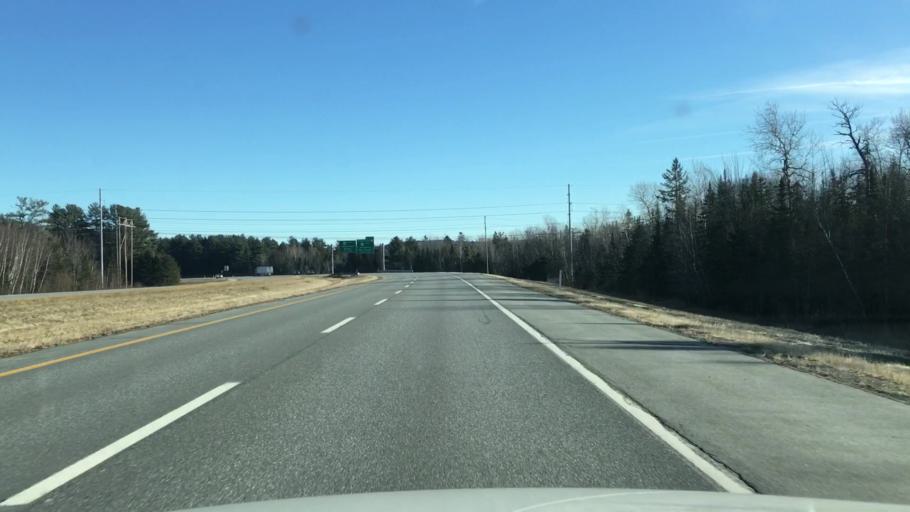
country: US
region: Maine
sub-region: Penobscot County
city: Brewer
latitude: 44.7693
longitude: -68.7374
